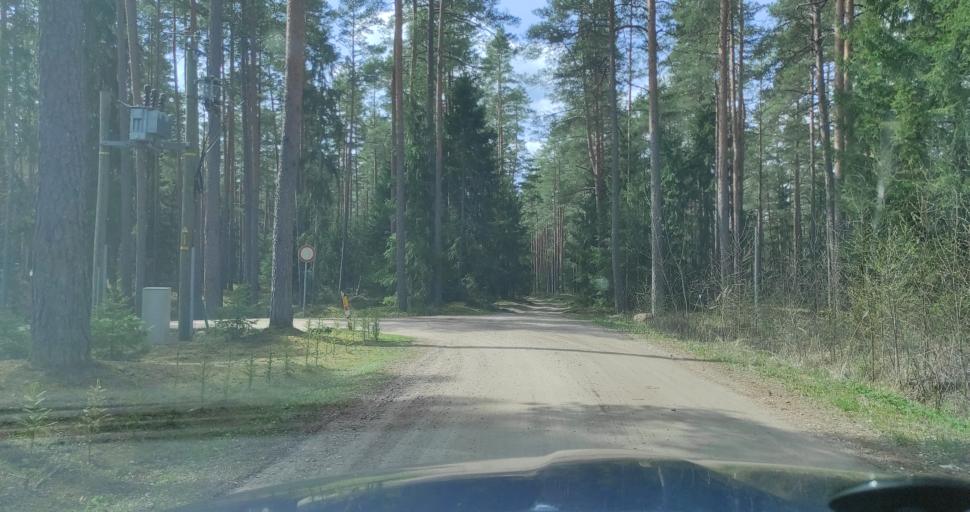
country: LV
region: Talsu Rajons
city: Stende
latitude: 57.2185
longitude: 22.2480
